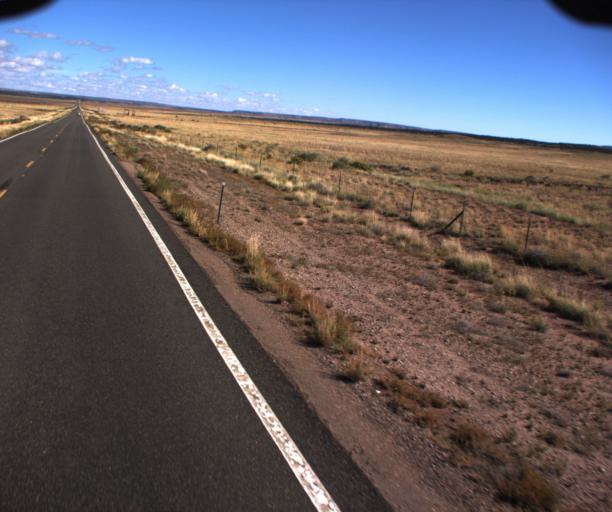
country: US
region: Arizona
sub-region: Apache County
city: Saint Johns
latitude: 34.6705
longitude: -109.2881
